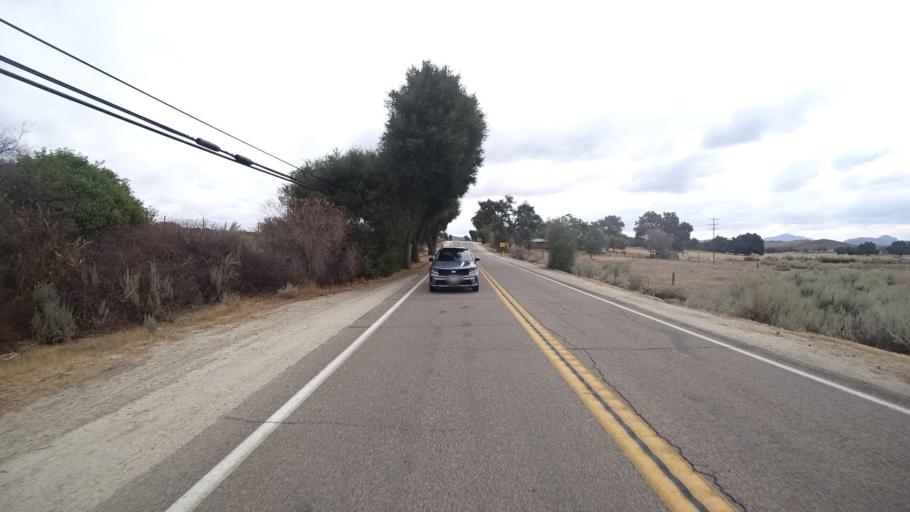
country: US
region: California
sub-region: San Diego County
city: Campo
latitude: 32.6420
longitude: -116.4838
